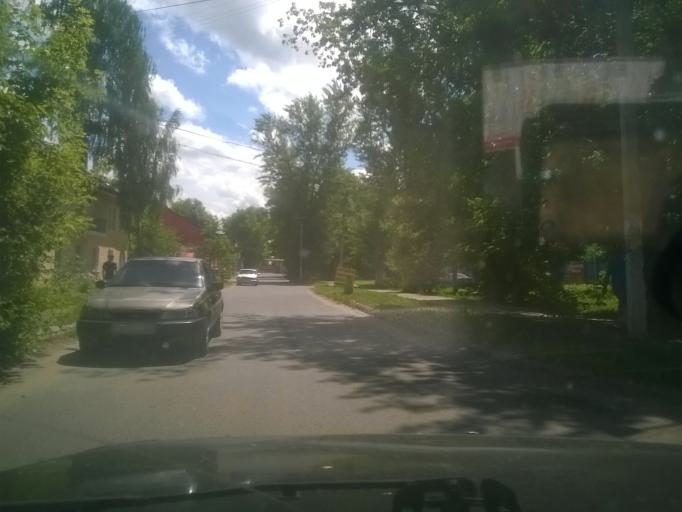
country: RU
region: Kursk
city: Voroshnevo
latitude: 51.6666
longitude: 36.1025
